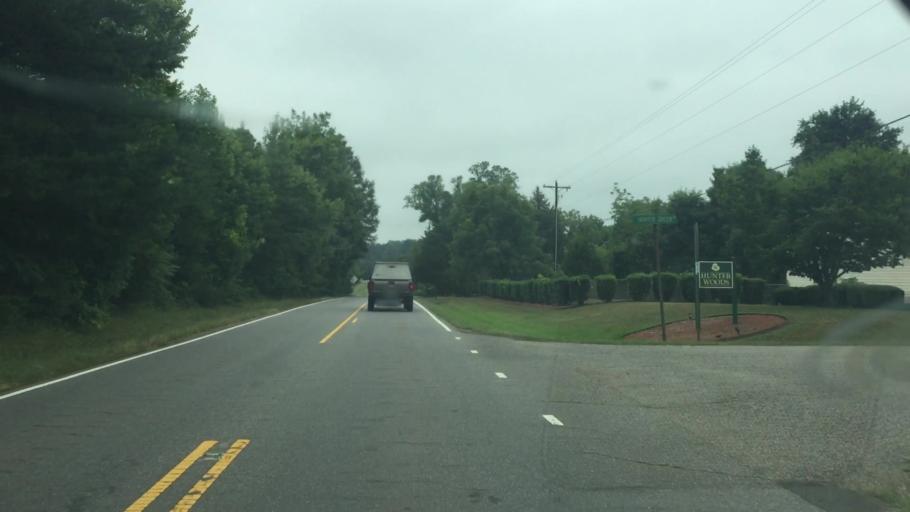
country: US
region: North Carolina
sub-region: Iredell County
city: Mooresville
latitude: 35.5244
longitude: -80.7699
